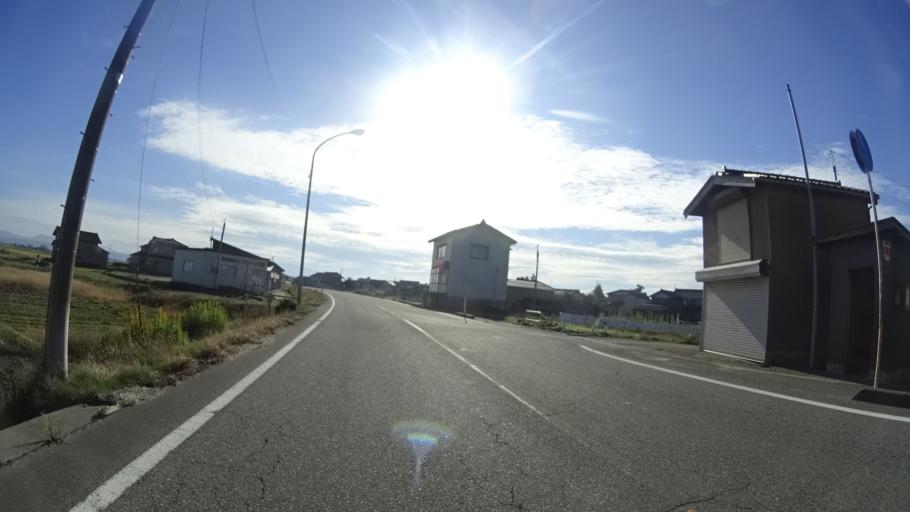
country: JP
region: Niigata
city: Mitsuke
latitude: 37.5766
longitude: 138.8359
